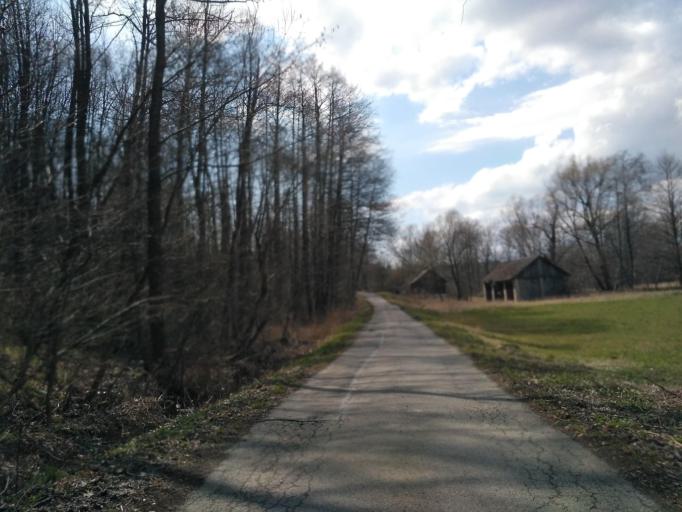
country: PL
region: Subcarpathian Voivodeship
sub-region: Powiat ropczycko-sedziszowski
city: Iwierzyce
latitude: 49.9936
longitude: 21.7403
